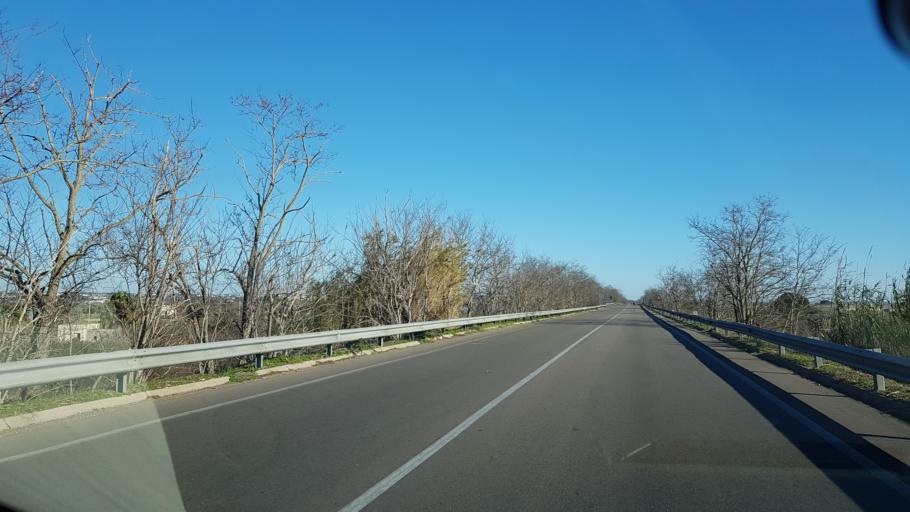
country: IT
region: Apulia
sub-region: Provincia di Lecce
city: Taviano
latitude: 39.9973
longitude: 18.0822
